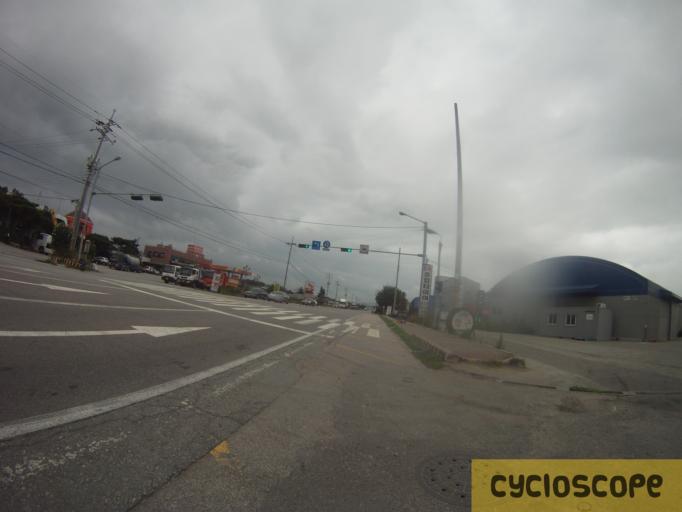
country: KR
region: Gyeonggi-do
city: Hwaseong-si
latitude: 37.0237
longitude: 126.8080
